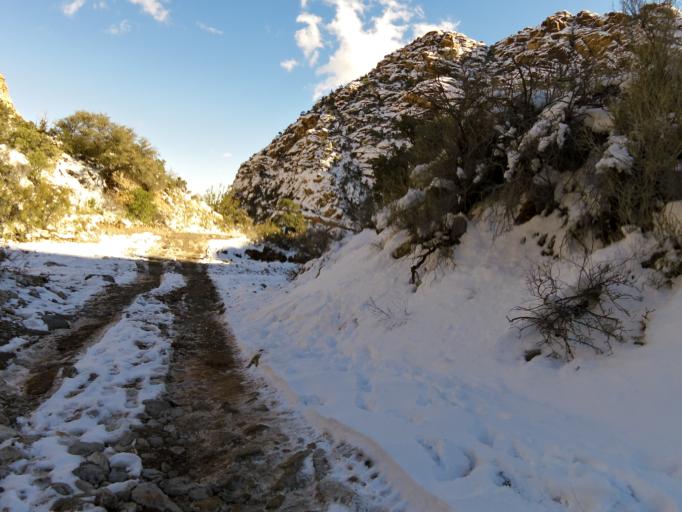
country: US
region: Nevada
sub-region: Clark County
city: Summerlin South
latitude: 36.1635
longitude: -115.5051
